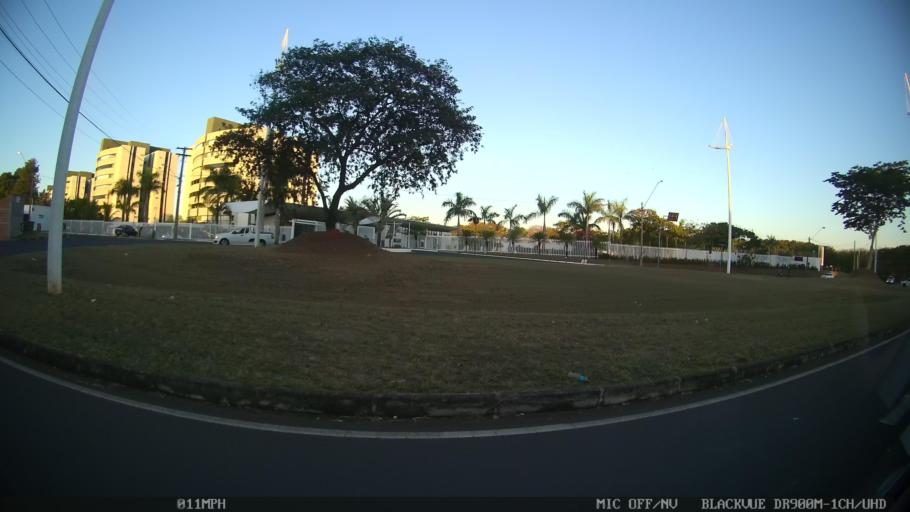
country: BR
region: Sao Paulo
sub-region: Sao Jose Do Rio Preto
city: Sao Jose do Rio Preto
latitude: -20.8529
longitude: -49.4051
